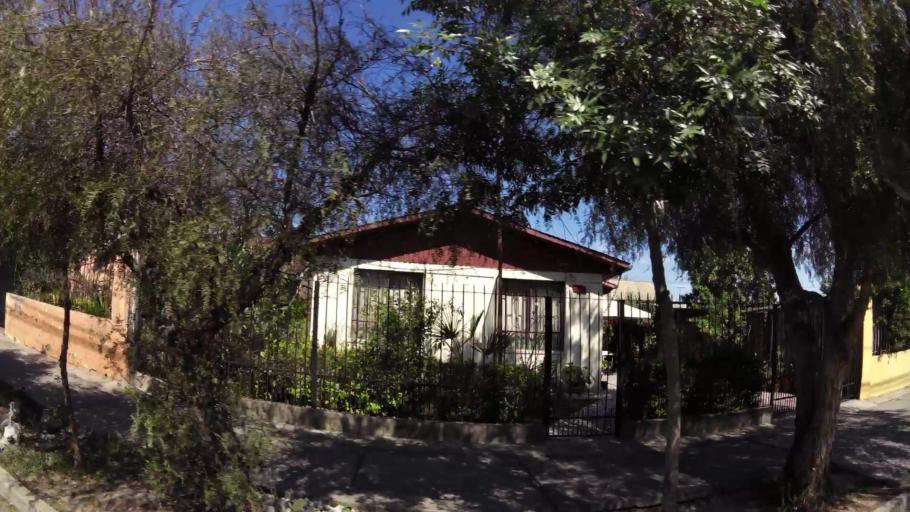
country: CL
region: Santiago Metropolitan
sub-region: Provincia de Santiago
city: La Pintana
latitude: -33.5375
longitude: -70.6610
